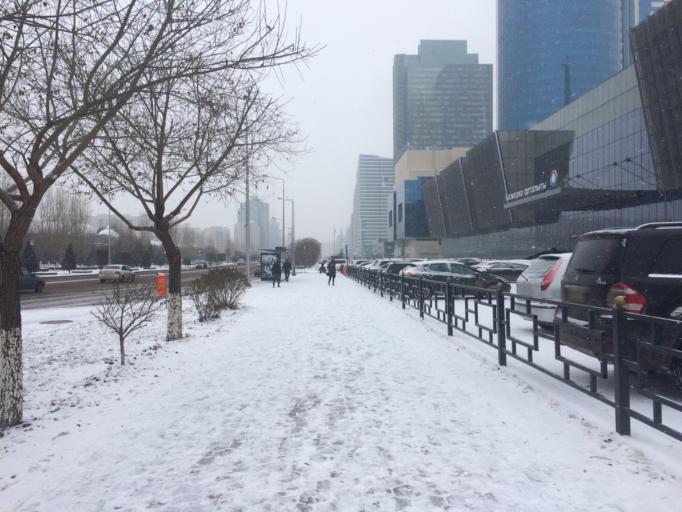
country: KZ
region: Astana Qalasy
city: Astana
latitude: 51.1324
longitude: 71.4187
